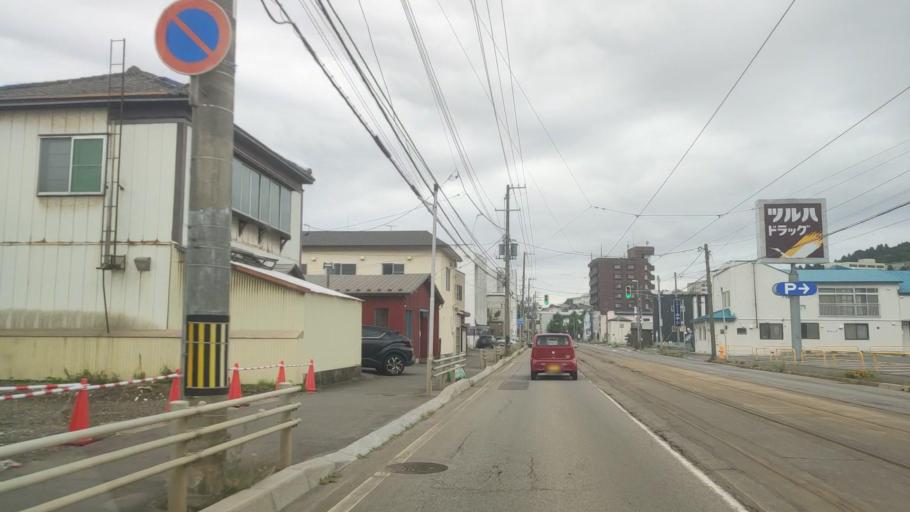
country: JP
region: Hokkaido
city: Hakodate
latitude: 41.7693
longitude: 140.7099
